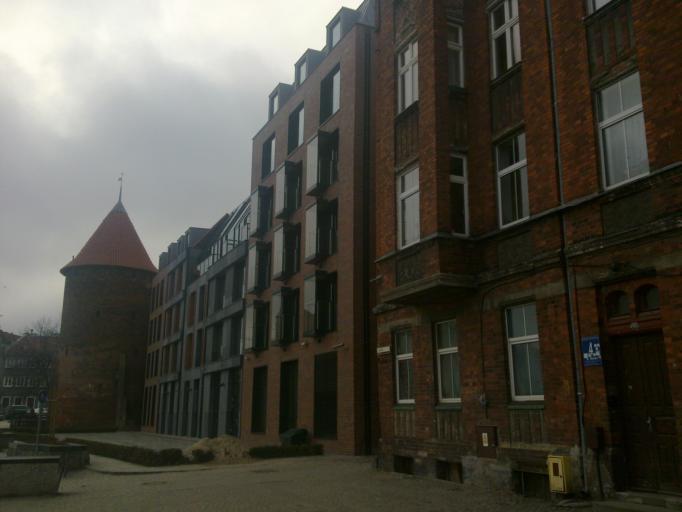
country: PL
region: Pomeranian Voivodeship
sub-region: Gdansk
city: Gdansk
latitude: 54.3534
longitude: 18.6588
